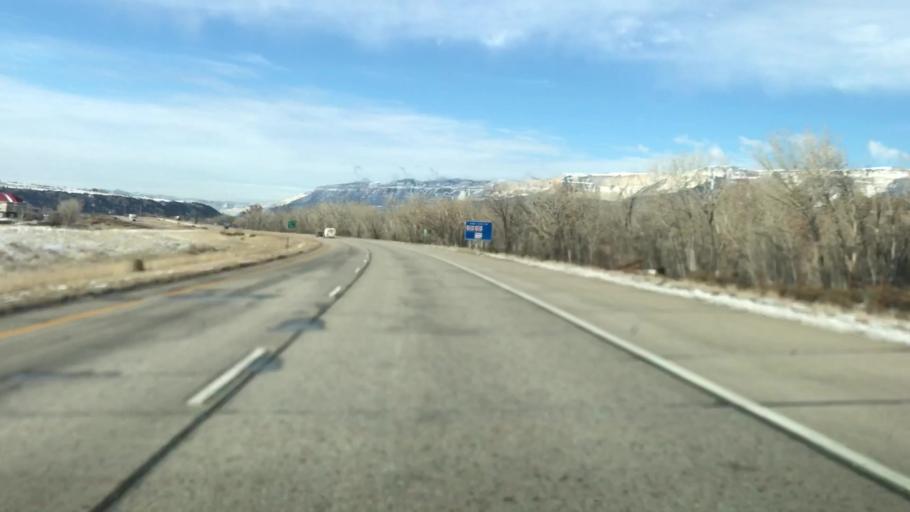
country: US
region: Colorado
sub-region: Garfield County
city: Rifle
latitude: 39.5265
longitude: -107.7672
